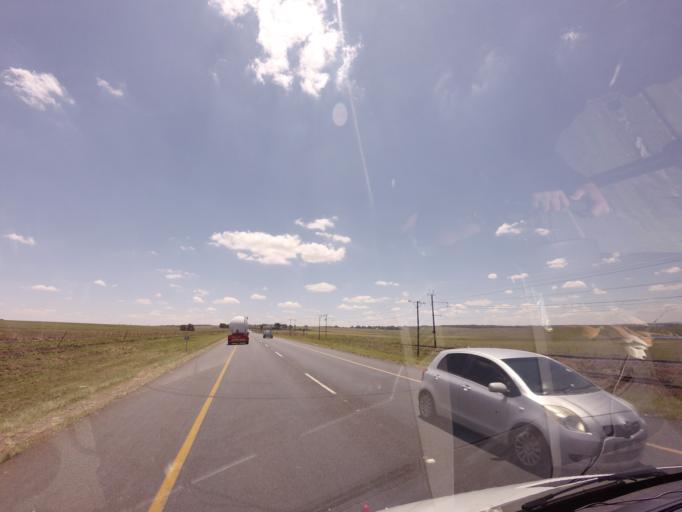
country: ZA
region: Mpumalanga
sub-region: Nkangala District Municipality
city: Belfast
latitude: -25.7302
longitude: 30.0983
